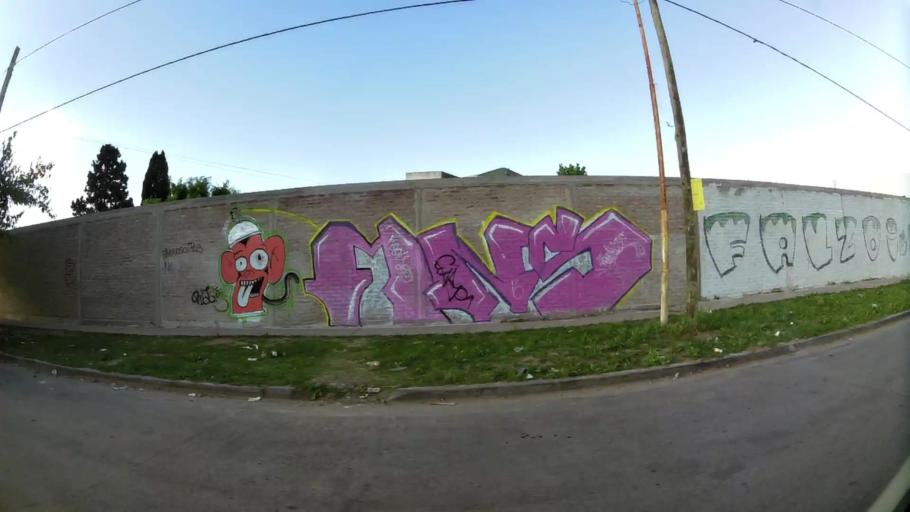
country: AR
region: Buenos Aires
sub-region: Partido de Moron
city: Moron
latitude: -34.6990
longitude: -58.6301
